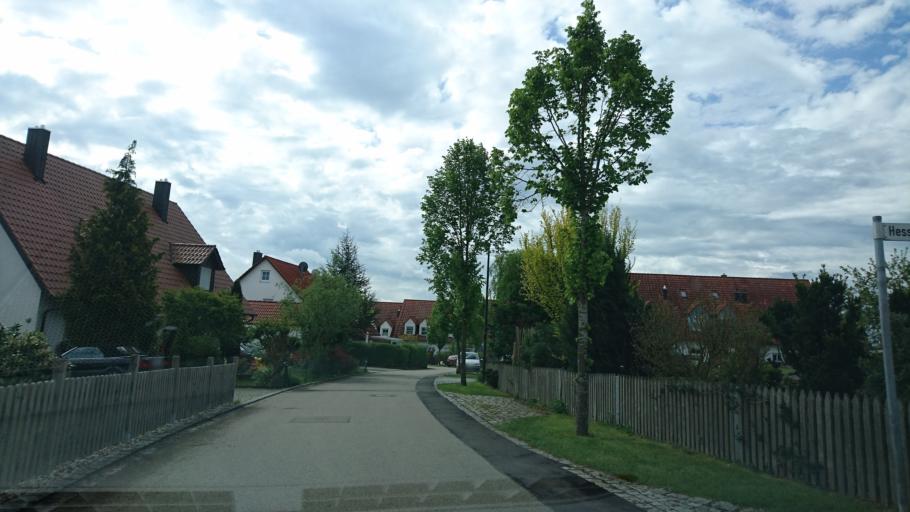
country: DE
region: Bavaria
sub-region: Swabia
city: Zusmarshausen
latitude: 48.4195
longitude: 10.5869
